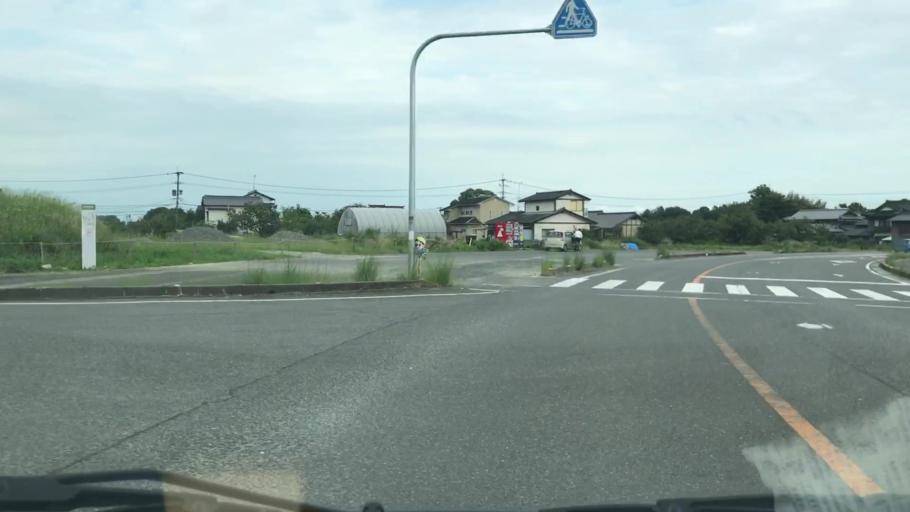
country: JP
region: Saga Prefecture
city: Saga-shi
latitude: 33.2884
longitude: 130.2490
